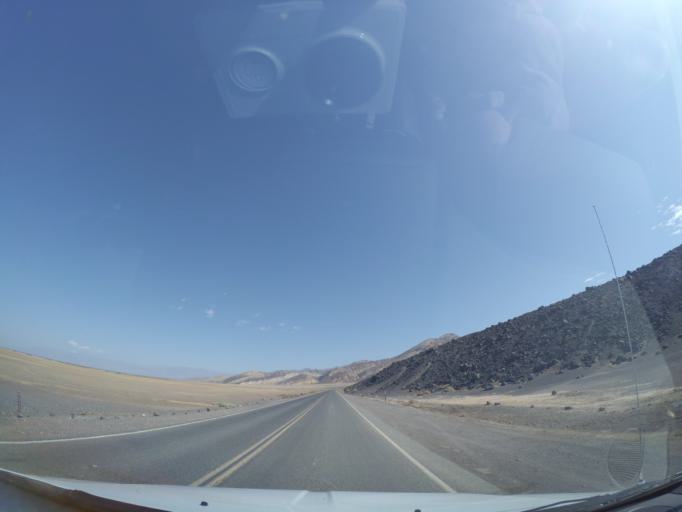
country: US
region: Nevada
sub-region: Nye County
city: Beatty
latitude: 36.3863
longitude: -116.8514
